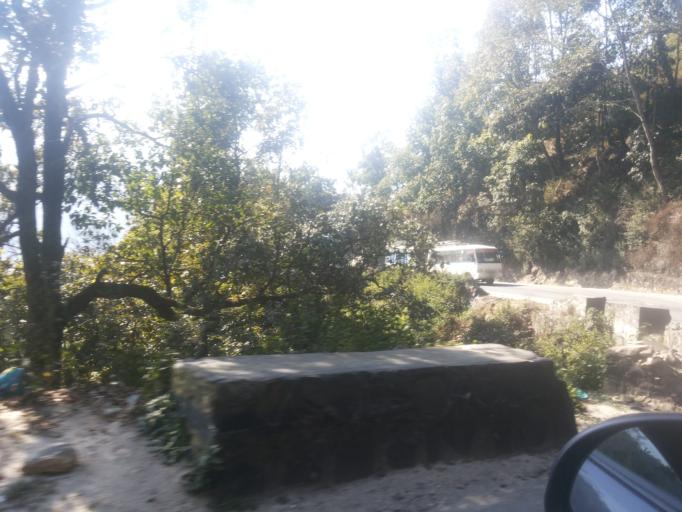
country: NP
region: Central Region
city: Kirtipur
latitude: 27.7136
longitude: 85.2035
